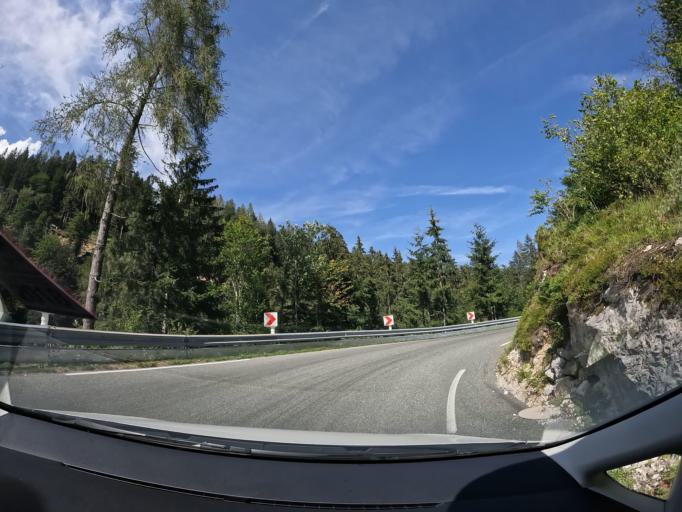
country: AT
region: Carinthia
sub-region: Politischer Bezirk Klagenfurt Land
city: Schiefling am See
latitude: 46.6106
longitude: 14.1057
